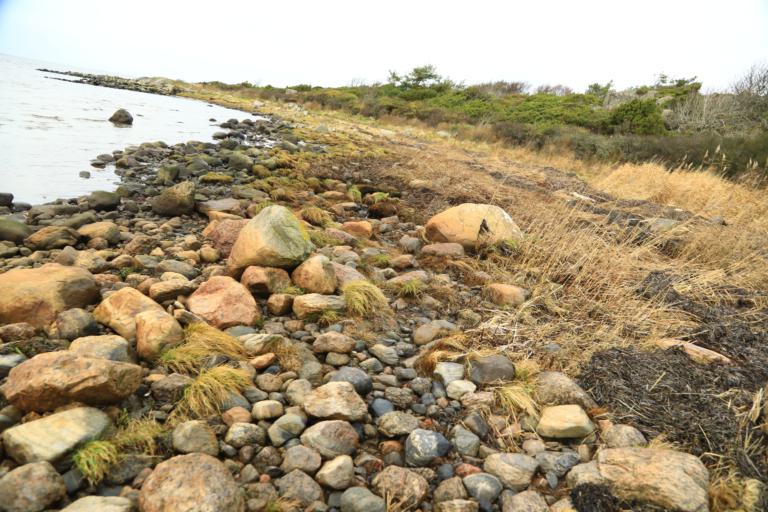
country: SE
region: Halland
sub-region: Varbergs Kommun
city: Varberg
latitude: 57.1775
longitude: 12.2050
